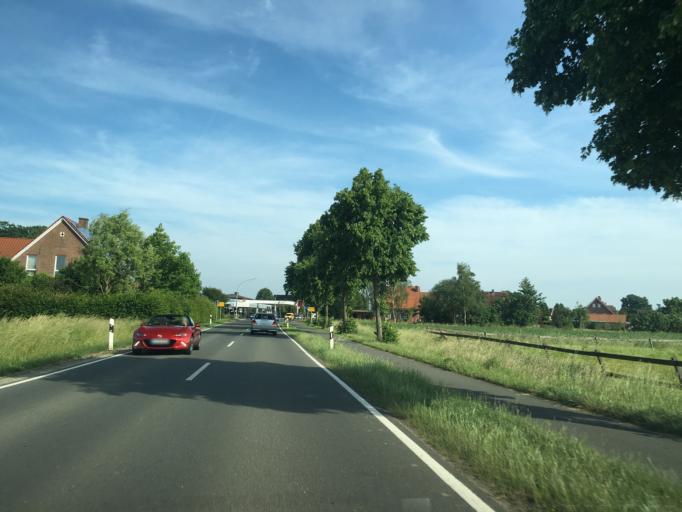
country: DE
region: North Rhine-Westphalia
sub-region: Regierungsbezirk Munster
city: Nordwalde
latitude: 52.0968
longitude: 7.4759
